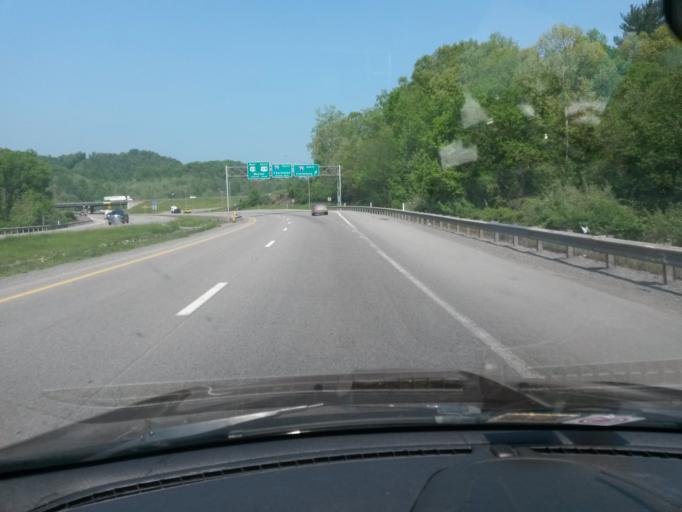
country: US
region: West Virginia
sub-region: Lewis County
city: Weston
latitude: 39.0212
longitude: -80.4226
